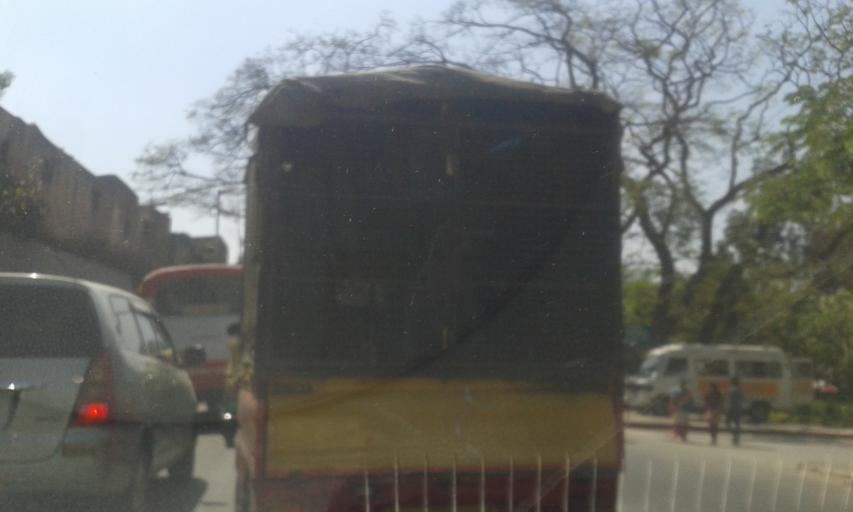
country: IN
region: Karnataka
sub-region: Bangalore Urban
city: Bangalore
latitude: 12.9730
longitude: 77.5665
